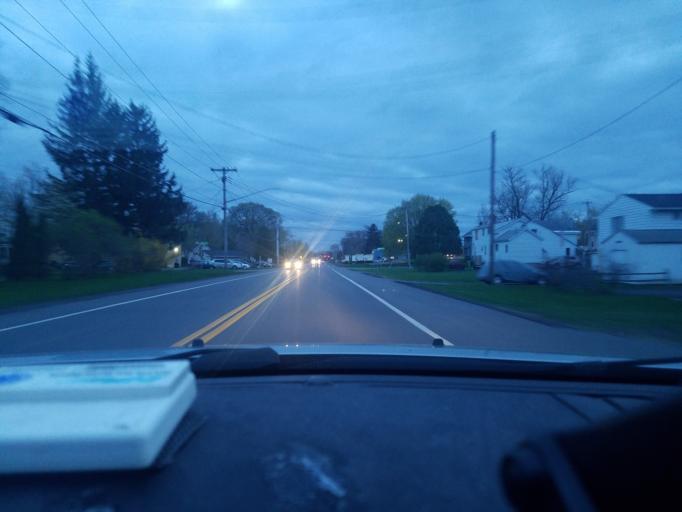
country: US
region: New York
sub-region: Onondaga County
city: North Syracuse
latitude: 43.1270
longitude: -76.1348
